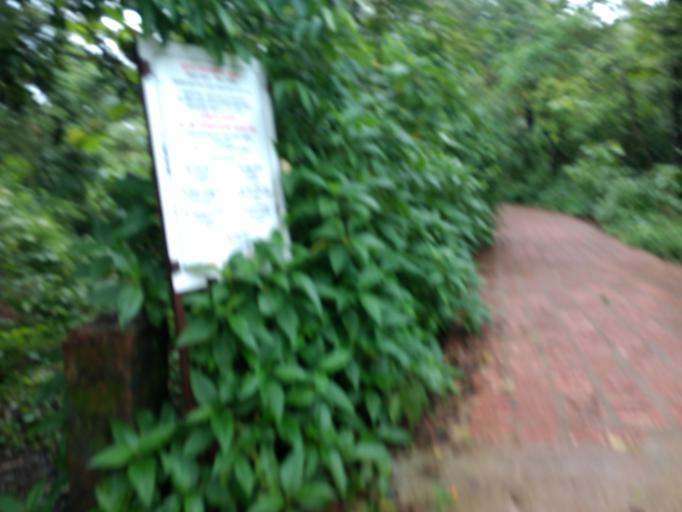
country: IN
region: Maharashtra
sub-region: Ratnagiri
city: Guhagar
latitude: 17.4957
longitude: 73.1886
